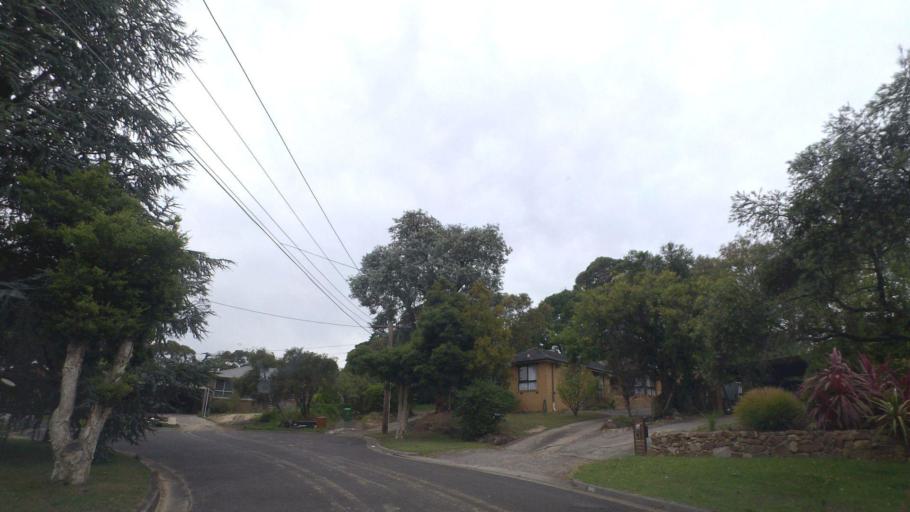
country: AU
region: Victoria
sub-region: Yarra Ranges
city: Kilsyth
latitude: -37.7999
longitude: 145.3262
